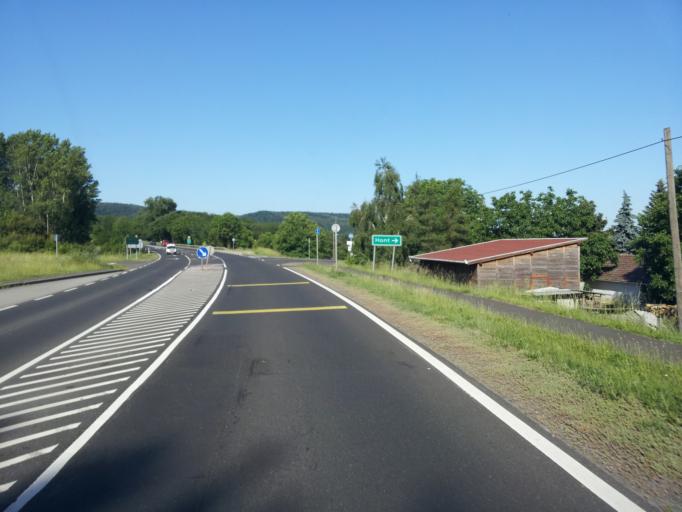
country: SK
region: Nitriansky
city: Sahy
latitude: 48.0529
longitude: 19.0055
